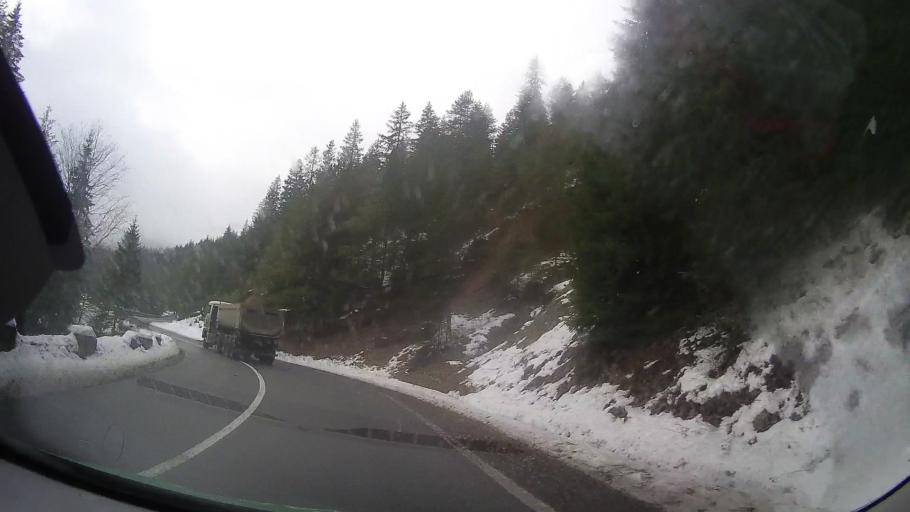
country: RO
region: Neamt
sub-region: Comuna Bicaz Chei
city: Bicaz Chei
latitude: 46.7800
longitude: 25.7584
